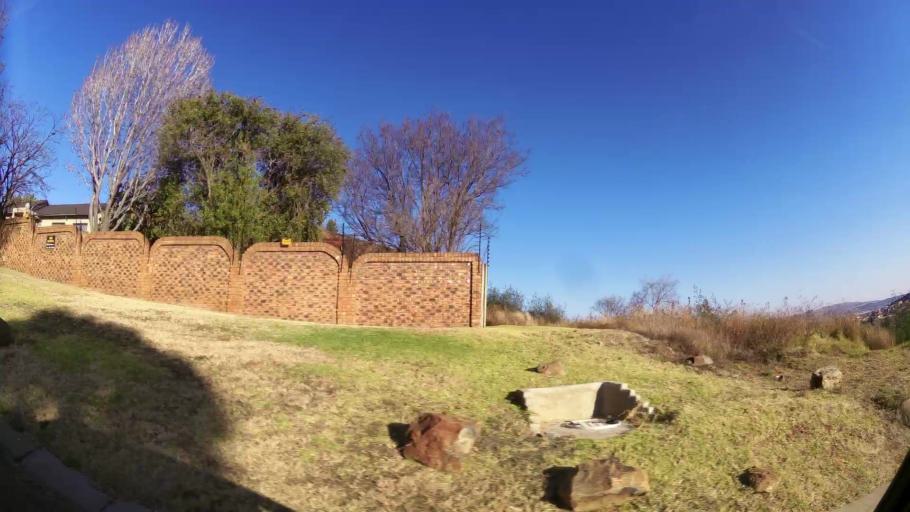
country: ZA
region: Gauteng
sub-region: City of Johannesburg Metropolitan Municipality
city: Johannesburg
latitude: -26.2977
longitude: 28.0748
